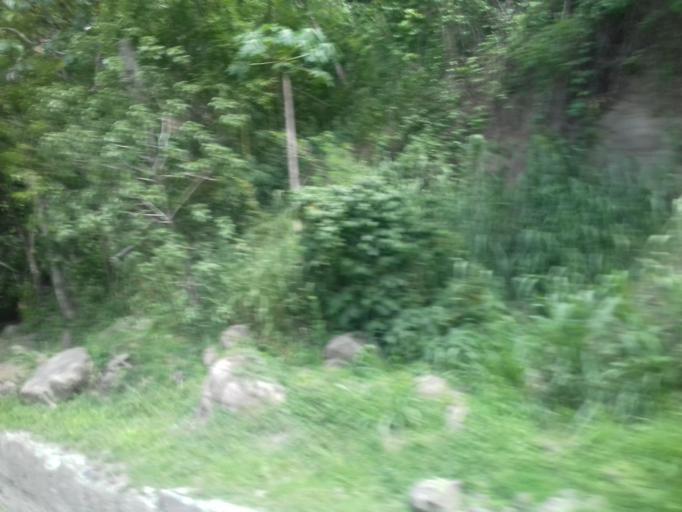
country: CO
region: Caldas
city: Supia
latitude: 5.3831
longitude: -75.6053
